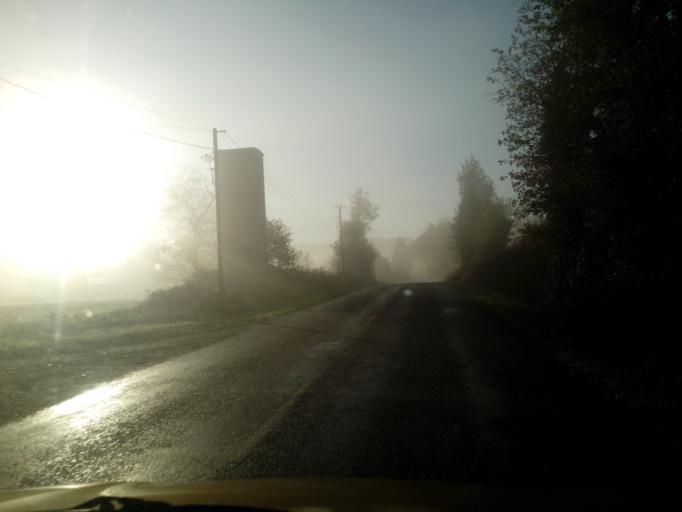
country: FR
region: Brittany
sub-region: Departement du Morbihan
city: Pluherlin
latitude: 47.7146
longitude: -2.3383
